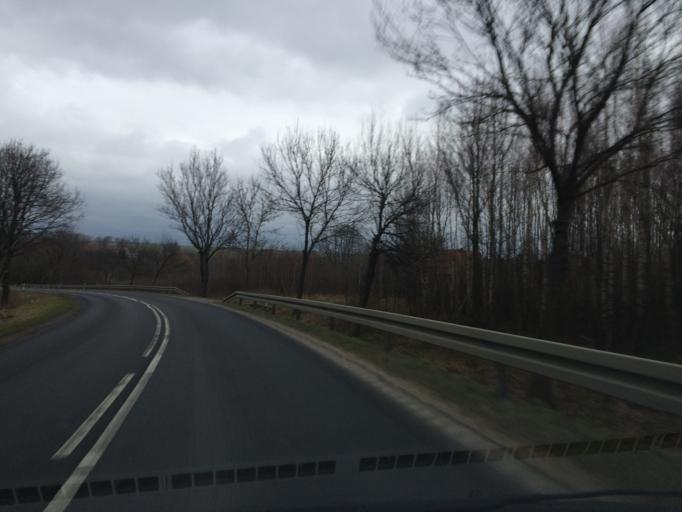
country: PL
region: Lower Silesian Voivodeship
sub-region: Powiat lubanski
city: Pisarzowice
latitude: 51.1631
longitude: 15.2678
